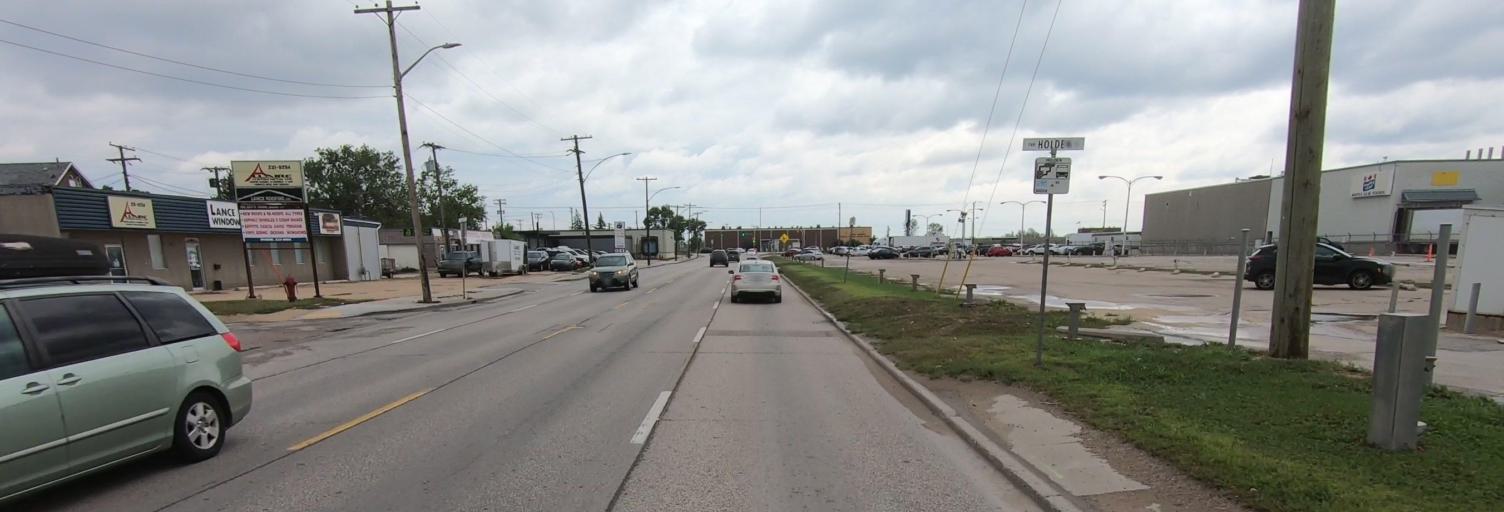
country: CA
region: Manitoba
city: Winnipeg
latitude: 49.8819
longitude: -97.0754
